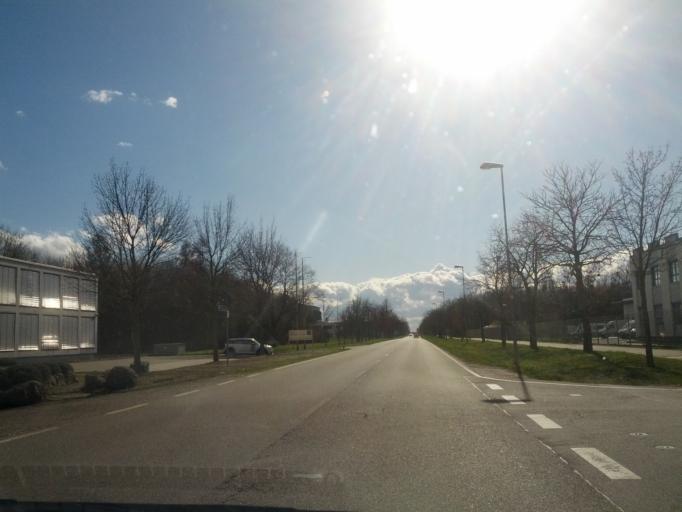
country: DE
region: Baden-Wuerttemberg
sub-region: Freiburg Region
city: Eschbach
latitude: 47.8953
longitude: 7.6224
